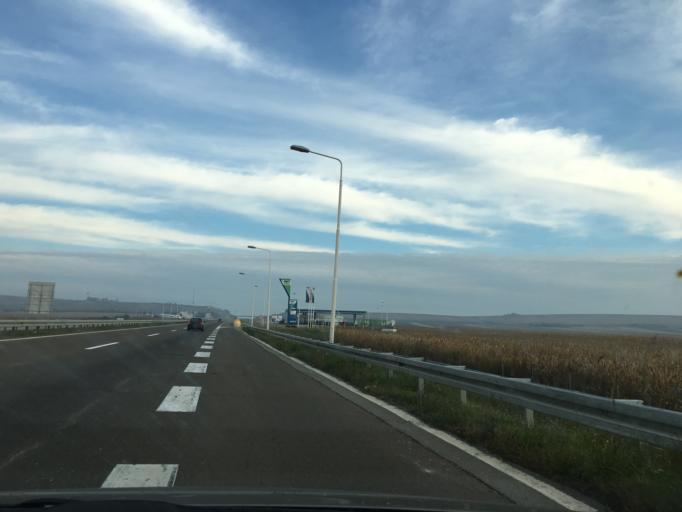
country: RS
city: Beska
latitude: 45.1440
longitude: 20.0848
